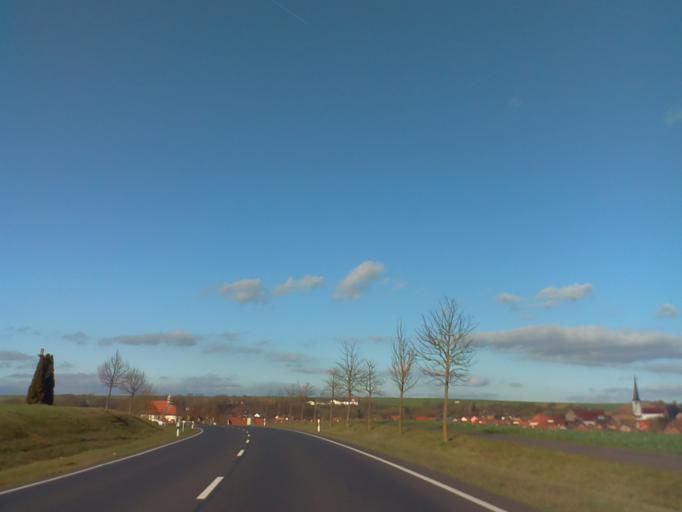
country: DE
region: Bavaria
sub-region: Regierungsbezirk Unterfranken
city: Wuelfershausen
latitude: 50.3249
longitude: 10.3433
